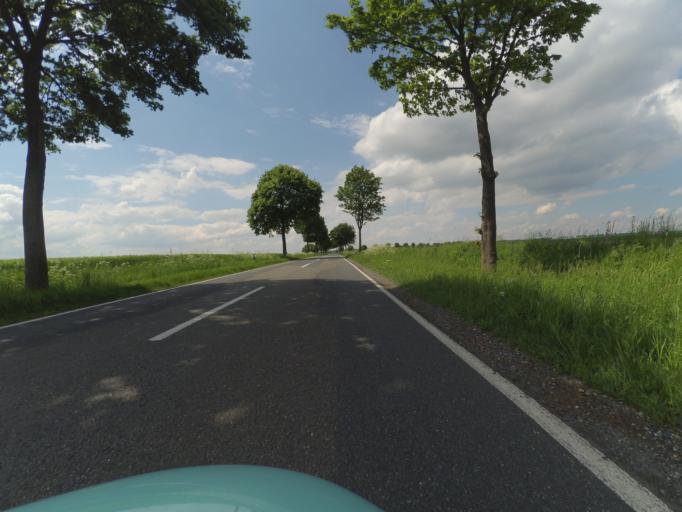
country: DE
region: Lower Saxony
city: Algermissen
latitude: 52.2514
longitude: 9.9410
